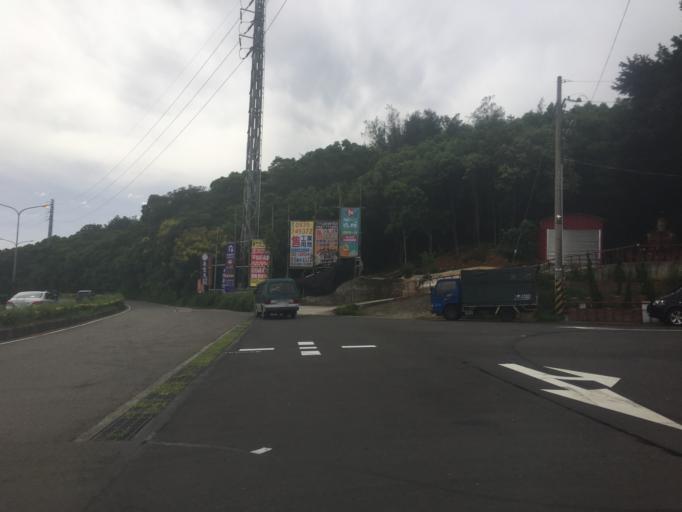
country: TW
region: Taiwan
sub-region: Hsinchu
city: Zhubei
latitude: 24.8783
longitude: 121.0275
